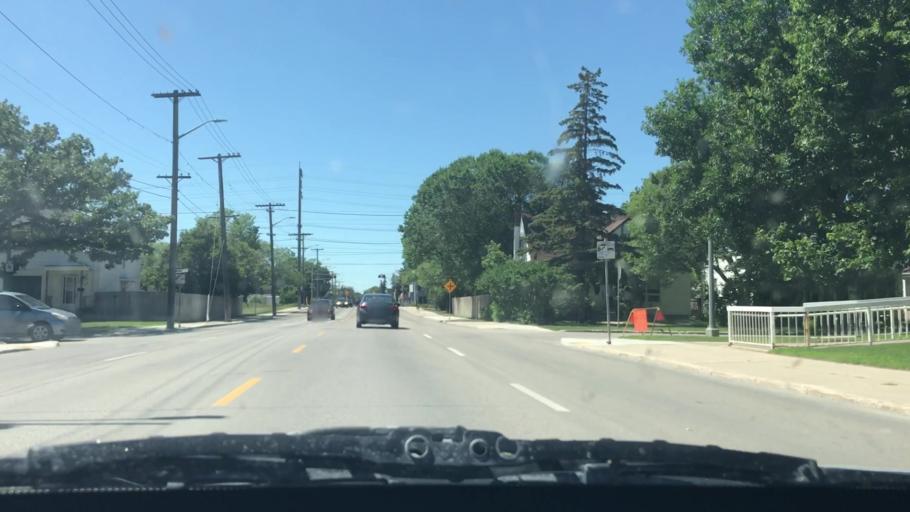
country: CA
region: Manitoba
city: Winnipeg
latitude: 49.8742
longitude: -97.1926
